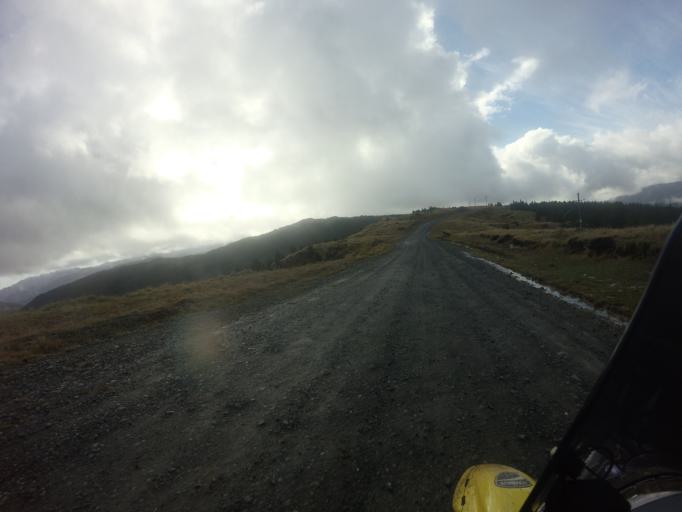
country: NZ
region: Gisborne
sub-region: Gisborne District
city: Gisborne
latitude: -38.1937
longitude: 177.8122
